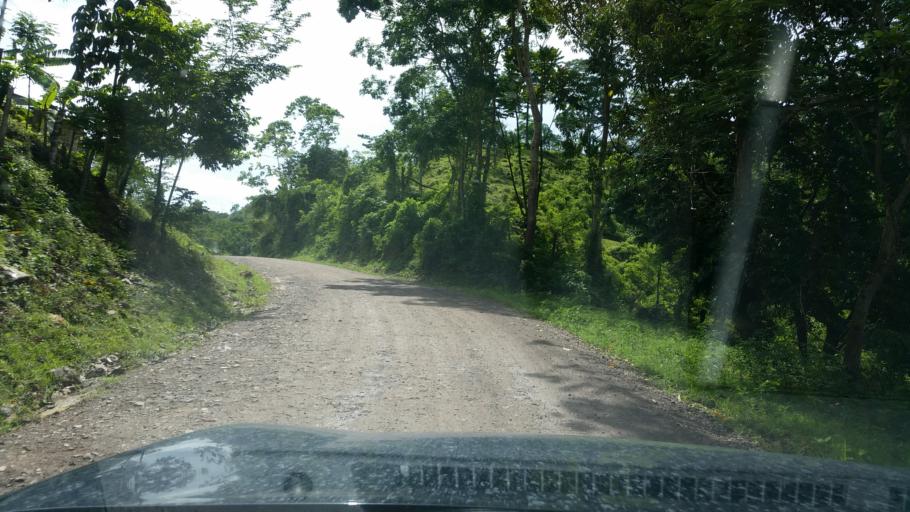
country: NI
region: Atlantico Norte (RAAN)
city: Siuna
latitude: 13.6816
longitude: -84.6407
